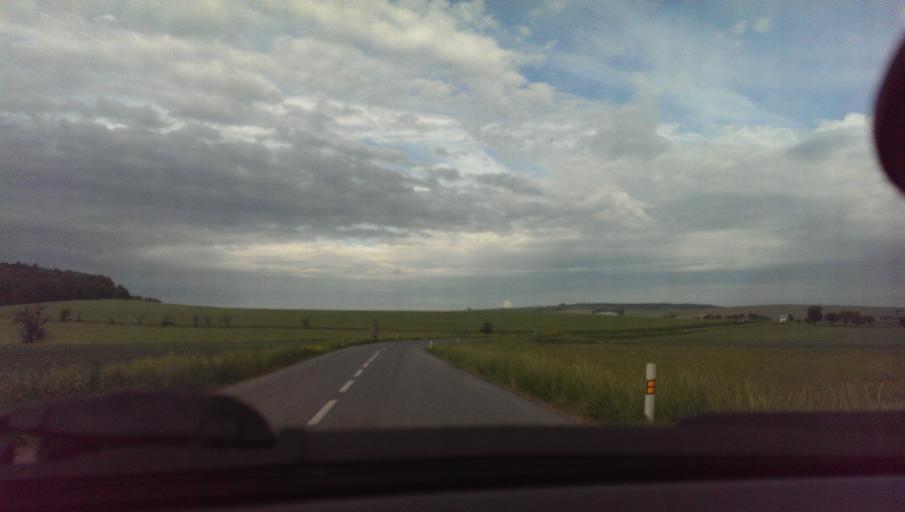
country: CZ
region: Zlin
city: Kvasice
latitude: 49.2485
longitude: 17.4532
